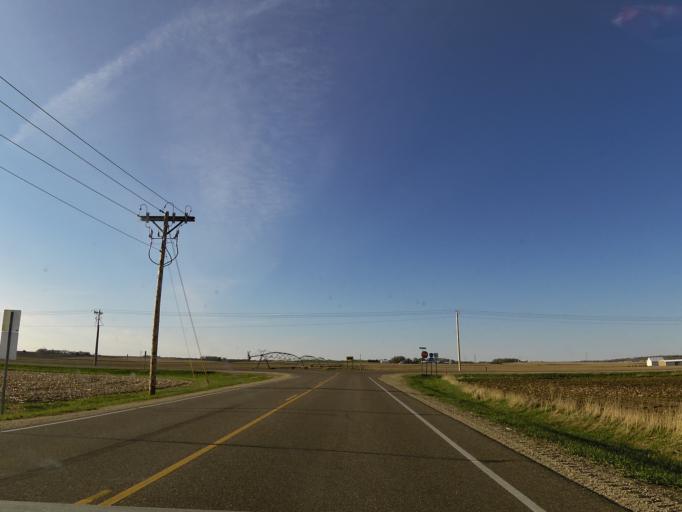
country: US
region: Minnesota
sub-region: Goodhue County
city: Cannon Falls
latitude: 44.5427
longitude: -93.0200
